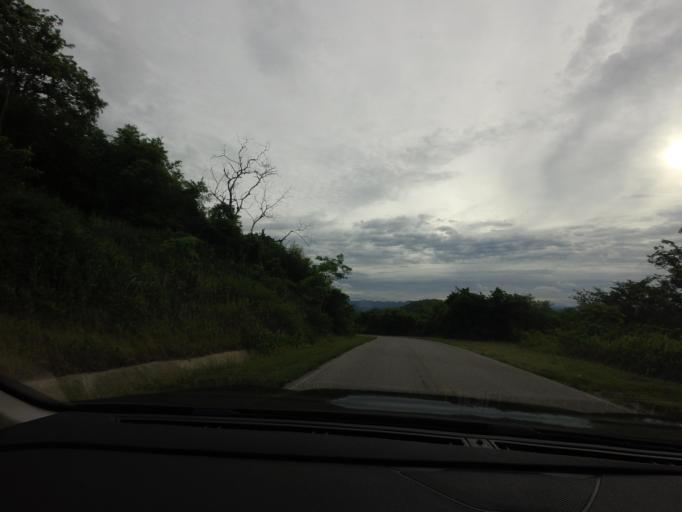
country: TH
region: Prachuap Khiri Khan
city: Hua Hin
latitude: 12.4930
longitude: 99.9444
